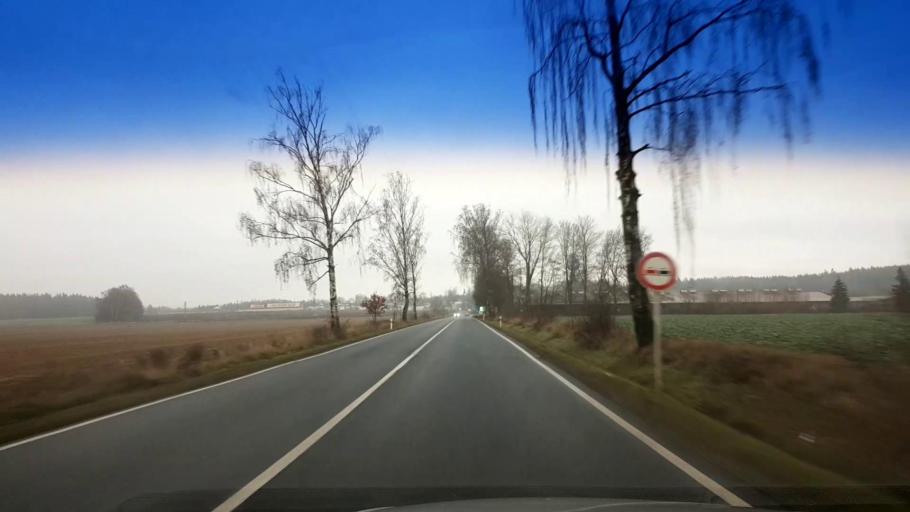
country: CZ
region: Karlovarsky
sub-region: Okres Cheb
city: Cheb
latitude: 50.0543
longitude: 12.3563
